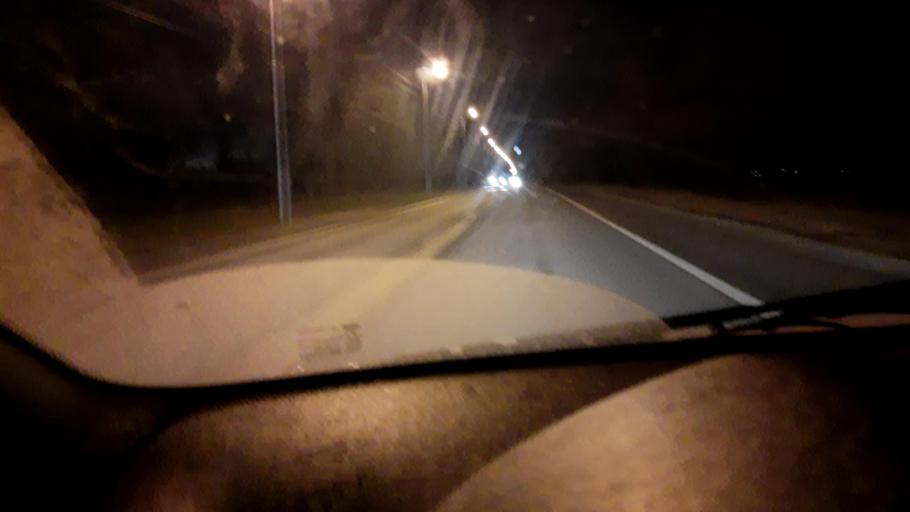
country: RU
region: Bashkortostan
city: Ufa
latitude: 54.8541
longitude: 56.1160
